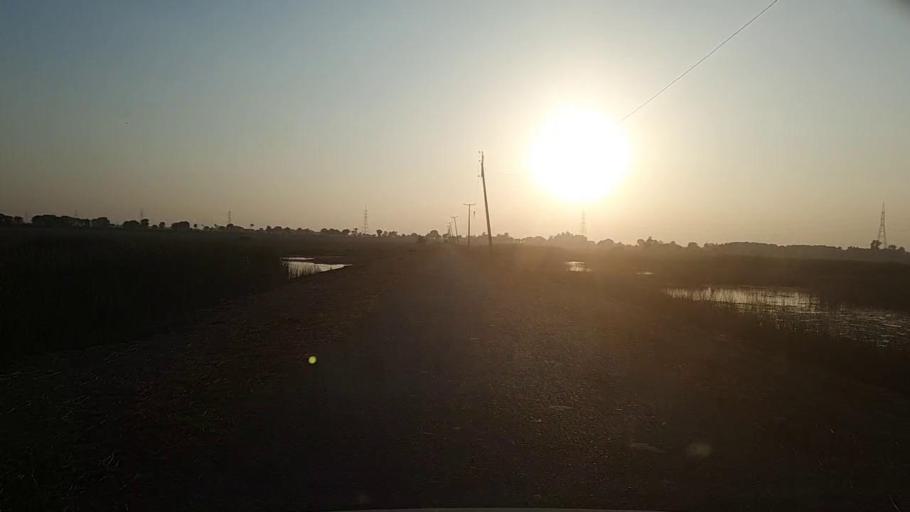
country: PK
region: Sindh
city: Mehar
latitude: 27.1915
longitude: 67.7468
